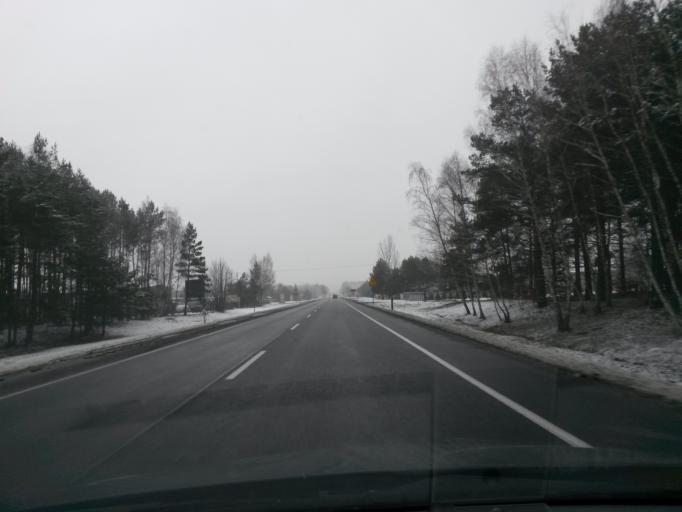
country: PL
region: Kujawsko-Pomorskie
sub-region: Powiat bydgoski
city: Biale Blota
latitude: 53.1202
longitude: 17.8824
